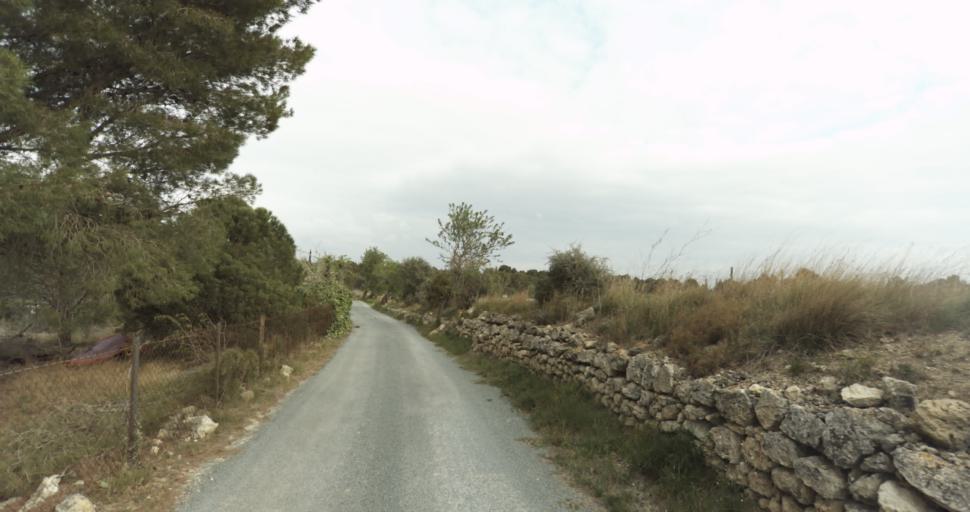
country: FR
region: Languedoc-Roussillon
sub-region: Departement de l'Aude
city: Leucate
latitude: 42.9301
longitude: 3.0252
